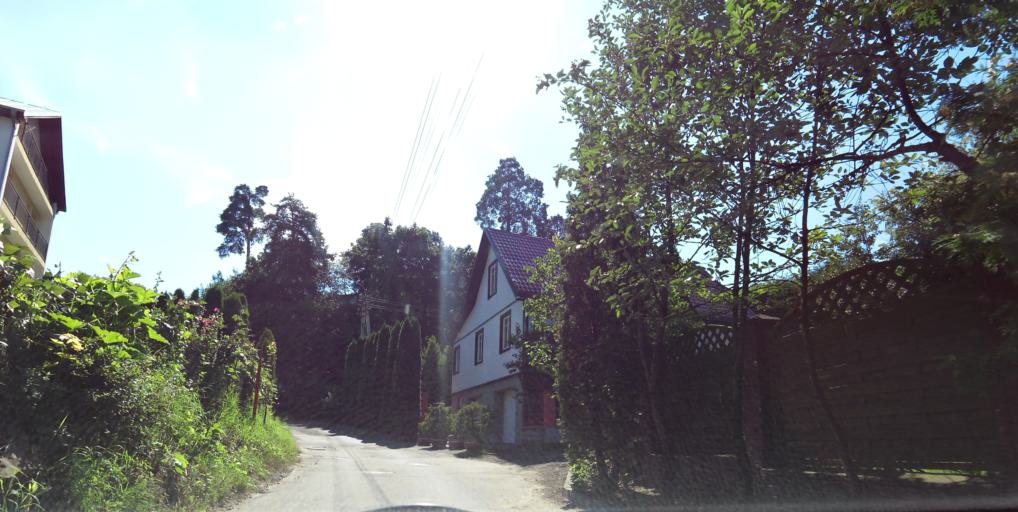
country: LT
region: Vilnius County
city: Rasos
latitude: 54.6921
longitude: 25.3122
